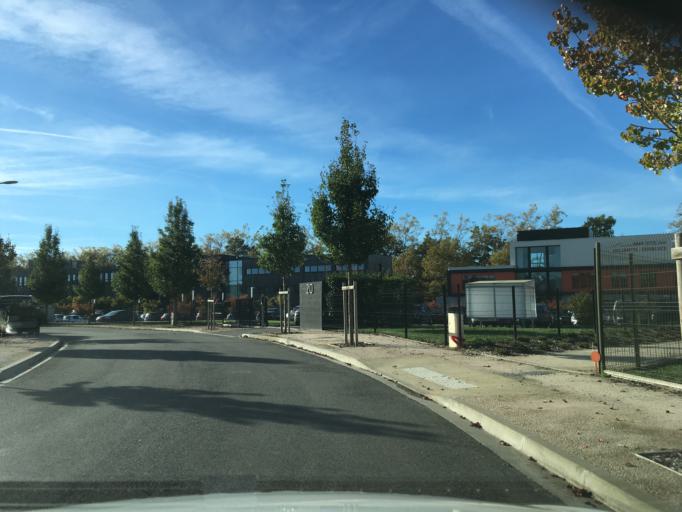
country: FR
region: Aquitaine
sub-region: Departement des Pyrenees-Atlantiques
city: Buros
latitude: 43.3216
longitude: -0.3097
